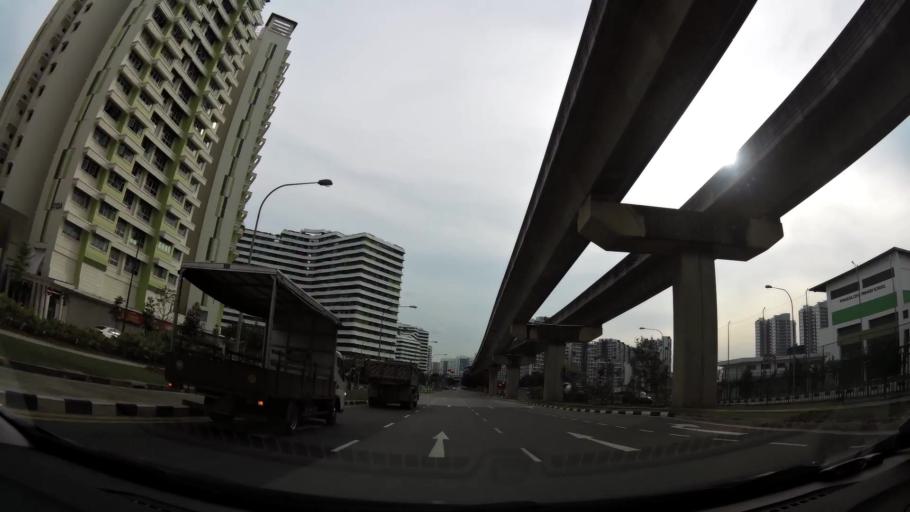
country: MY
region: Johor
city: Kampung Pasir Gudang Baru
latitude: 1.4114
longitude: 103.9003
